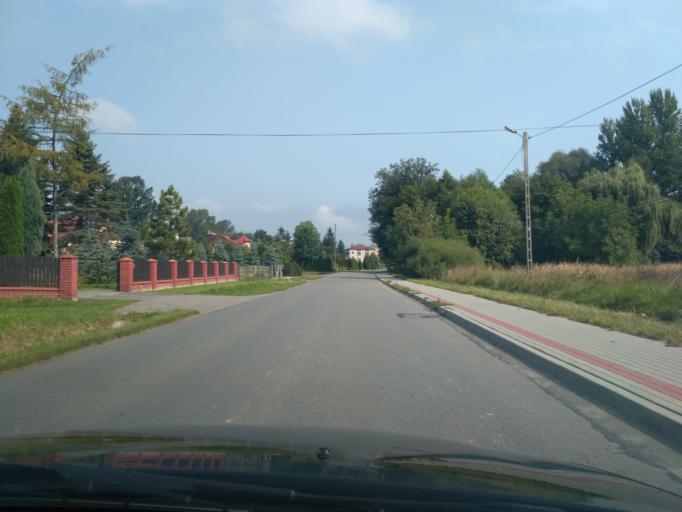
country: PL
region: Subcarpathian Voivodeship
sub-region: Powiat rzeszowski
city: Niechobrz
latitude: 49.9879
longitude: 21.8752
